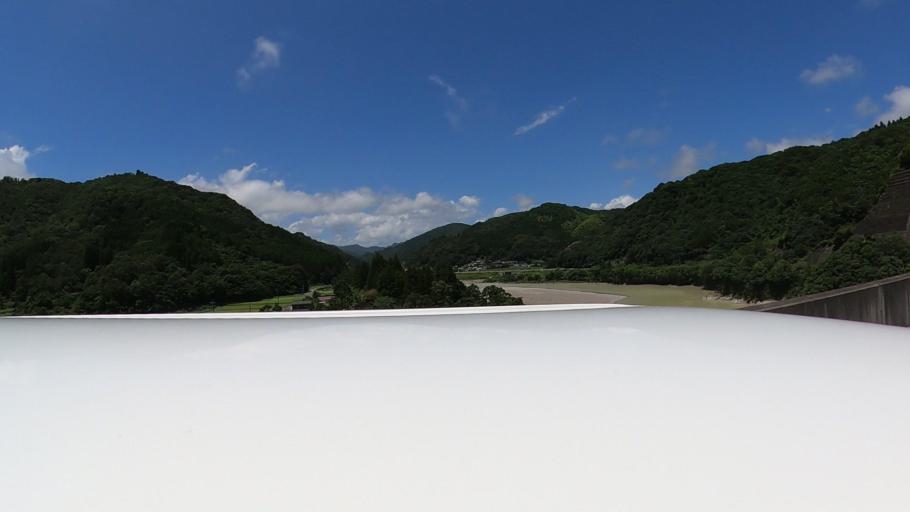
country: JP
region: Miyazaki
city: Takanabe
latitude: 32.3431
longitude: 131.5986
